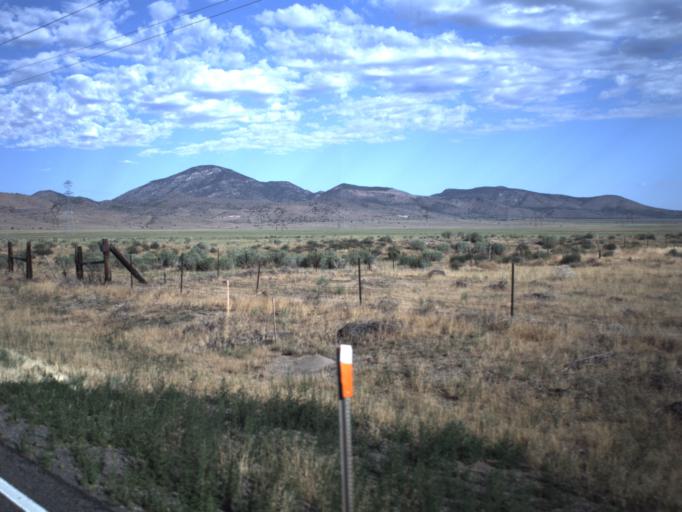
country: US
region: Utah
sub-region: Utah County
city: Genola
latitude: 39.9519
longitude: -111.9638
